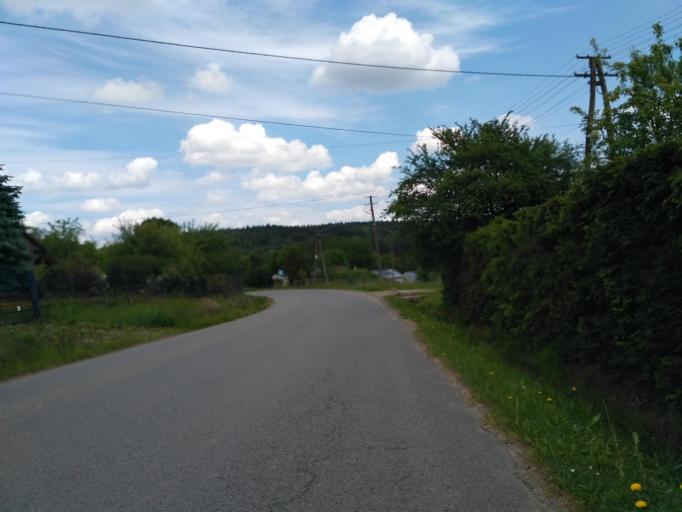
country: PL
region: Subcarpathian Voivodeship
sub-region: Powiat krosnienski
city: Chorkowka
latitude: 49.6151
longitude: 21.6472
